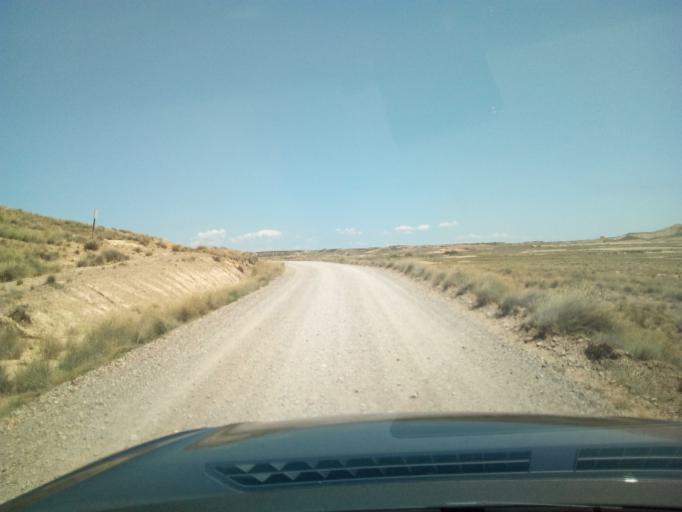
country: ES
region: Navarre
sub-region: Provincia de Navarra
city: Fustinana
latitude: 42.1711
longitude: -1.4205
